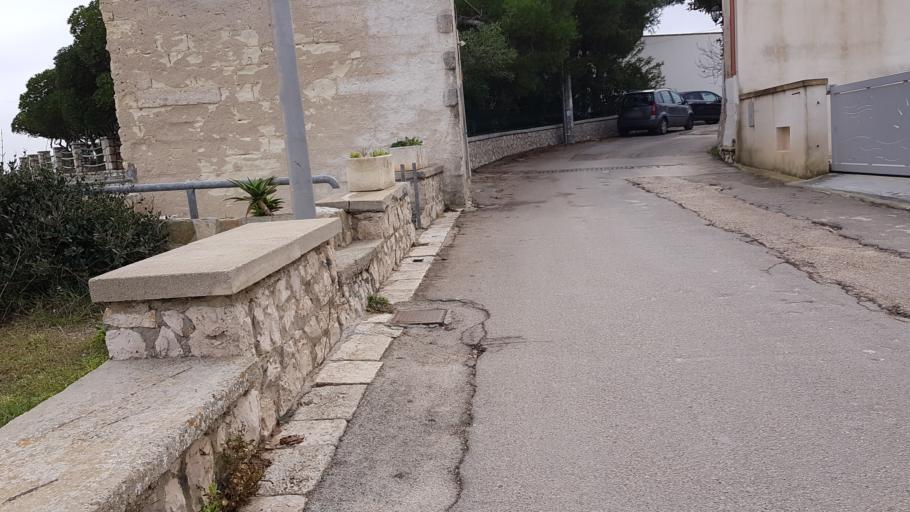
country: IT
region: Apulia
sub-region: Provincia di Lecce
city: Uggiano la Chiesa
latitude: 40.0803
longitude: 18.4836
